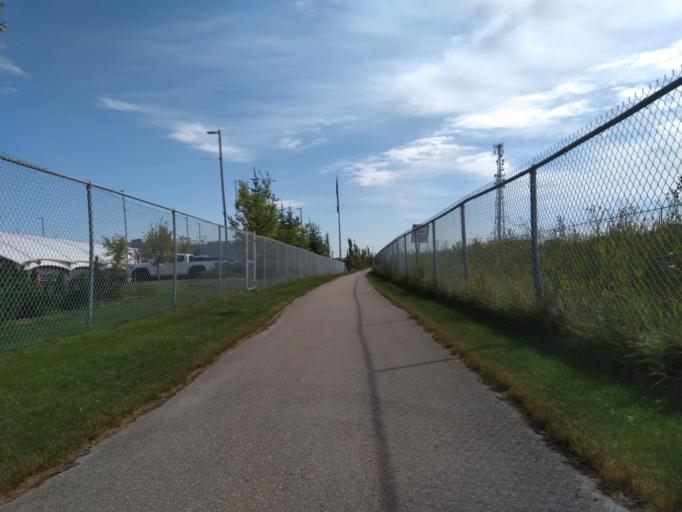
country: CA
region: Alberta
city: Calgary
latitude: 51.1521
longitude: -114.1931
